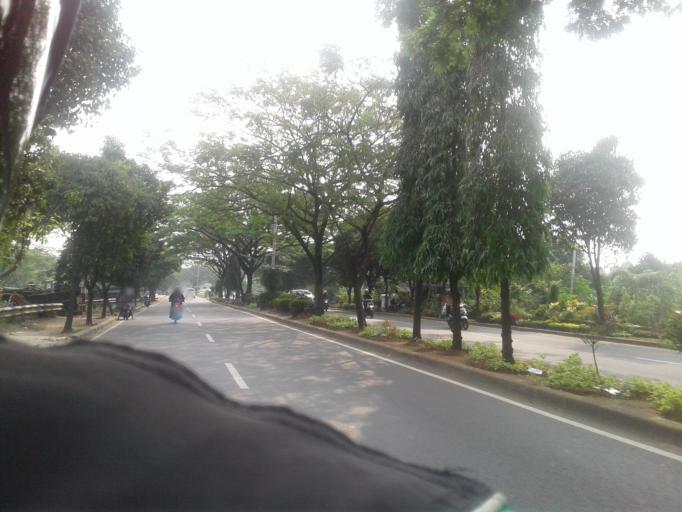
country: ID
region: West Java
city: Depok
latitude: -6.3812
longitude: 106.8589
